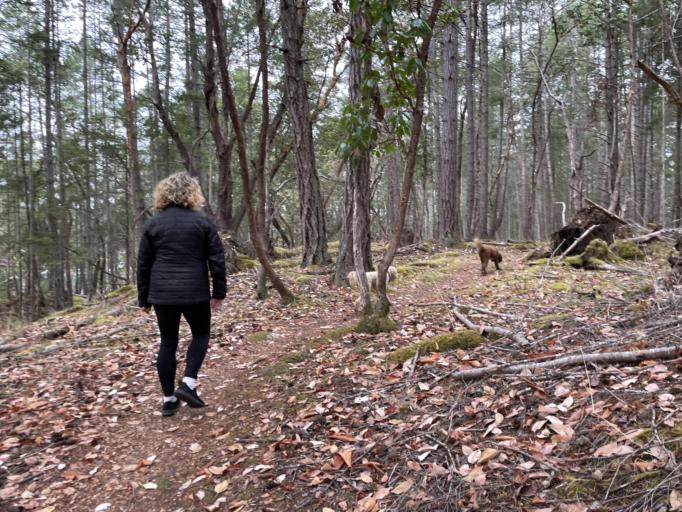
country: CA
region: British Columbia
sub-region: Cowichan Valley Regional District
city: Ladysmith
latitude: 49.0967
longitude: -123.7270
